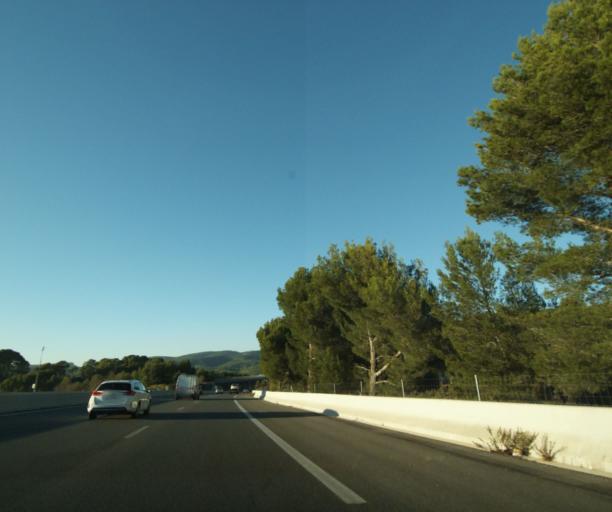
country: FR
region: Provence-Alpes-Cote d'Azur
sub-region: Departement des Bouches-du-Rhone
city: Ceyreste
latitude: 43.2008
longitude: 5.6343
